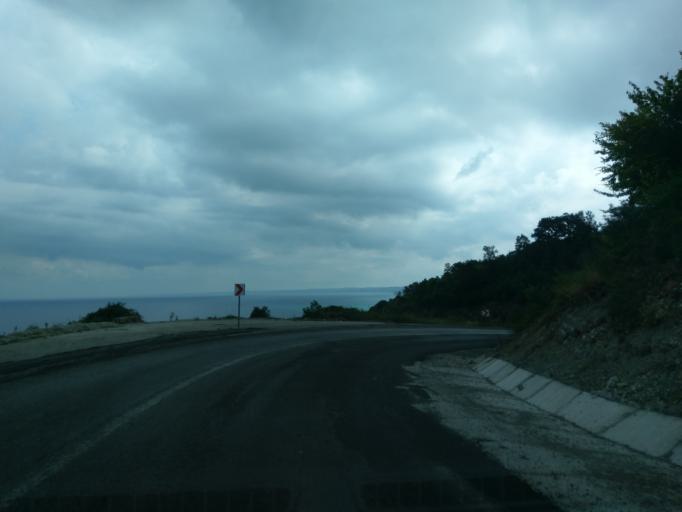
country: TR
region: Sinop
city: Ayancik
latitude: 41.9416
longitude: 34.6764
